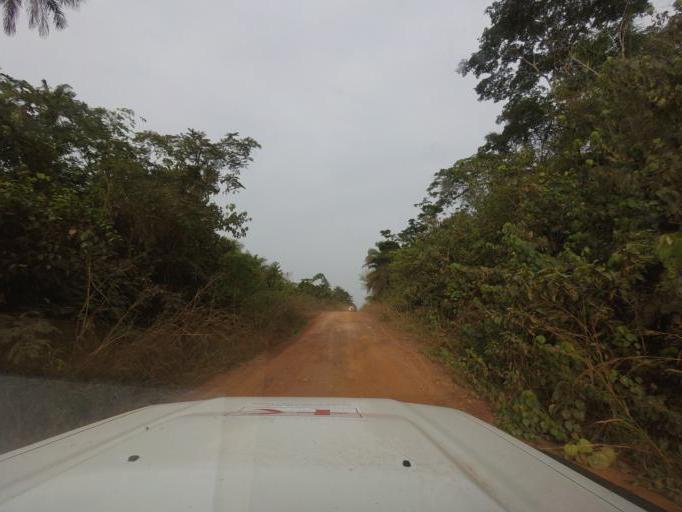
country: LR
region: Lofa
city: Voinjama
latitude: 8.3724
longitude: -9.8953
